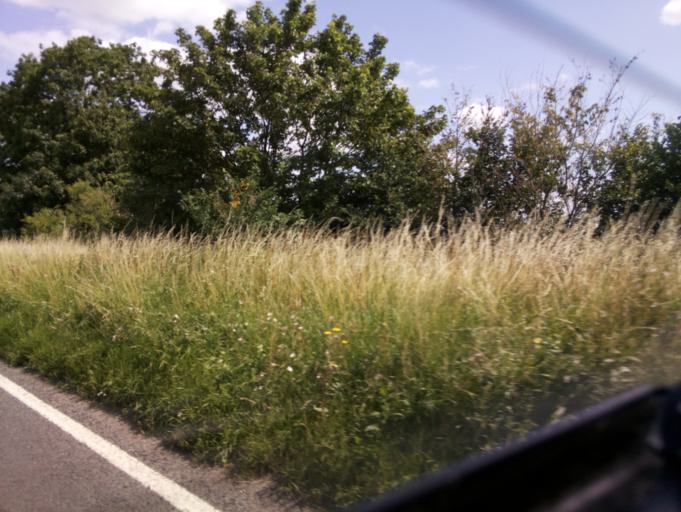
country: GB
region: England
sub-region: Buckinghamshire
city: Winslow
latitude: 51.8864
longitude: -0.8394
